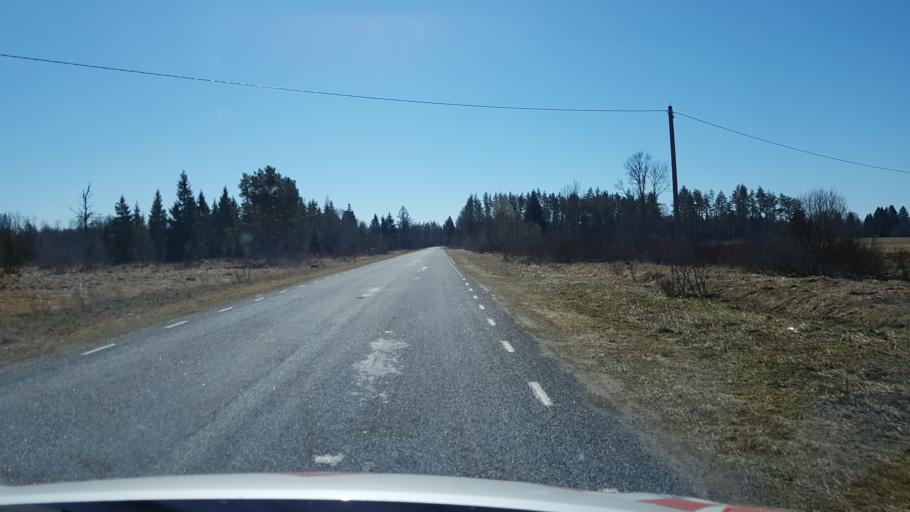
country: EE
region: Laeaene-Virumaa
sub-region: Haljala vald
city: Haljala
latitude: 59.4910
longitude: 26.2456
